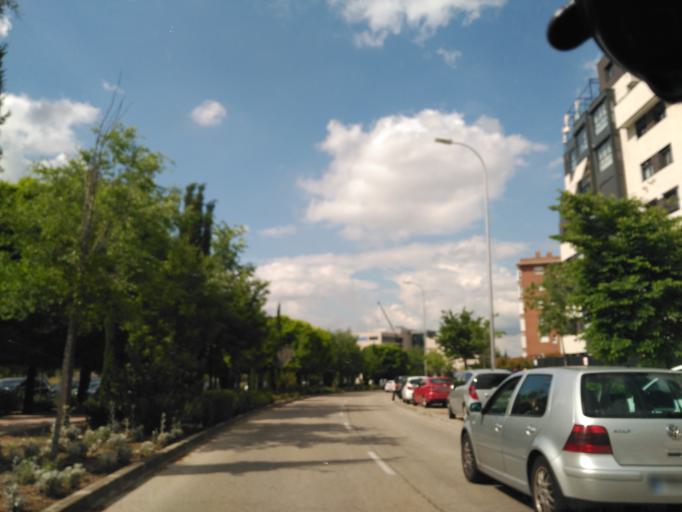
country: ES
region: Madrid
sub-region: Provincia de Madrid
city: Pinar de Chamartin
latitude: 40.4927
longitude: -3.6659
